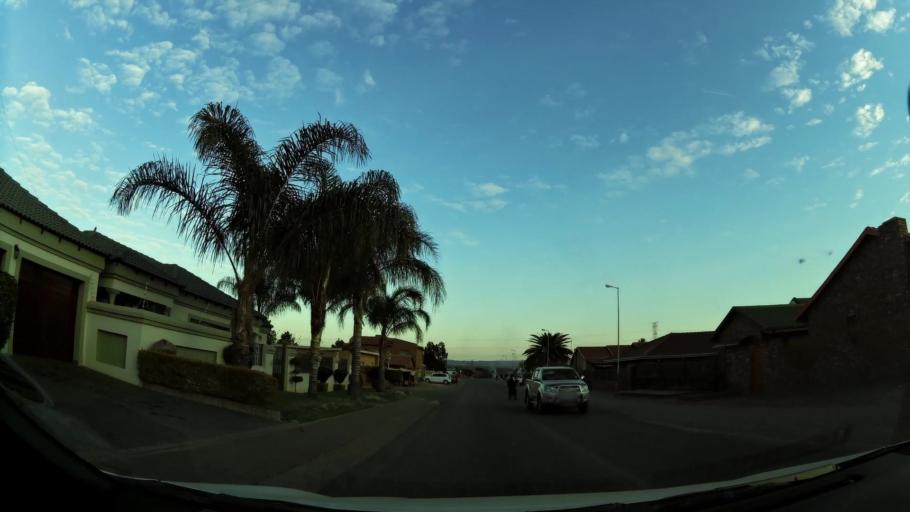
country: ZA
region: Gauteng
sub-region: City of Tshwane Metropolitan Municipality
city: Pretoria
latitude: -25.7166
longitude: 28.3450
